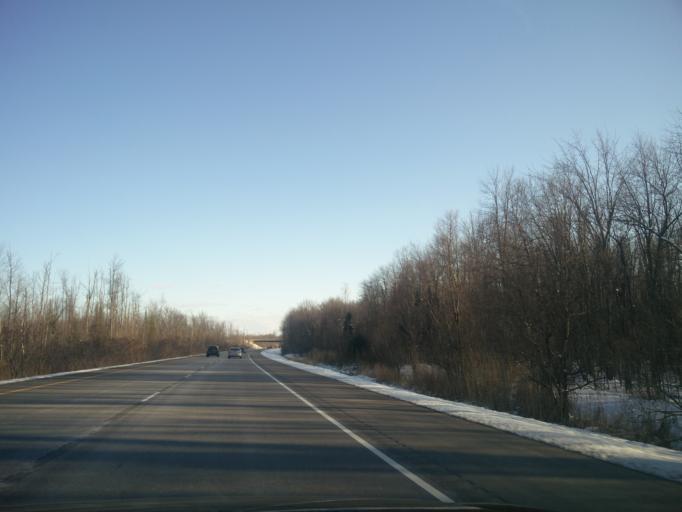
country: CA
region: Ontario
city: Prescott
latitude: 44.8220
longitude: -75.5197
